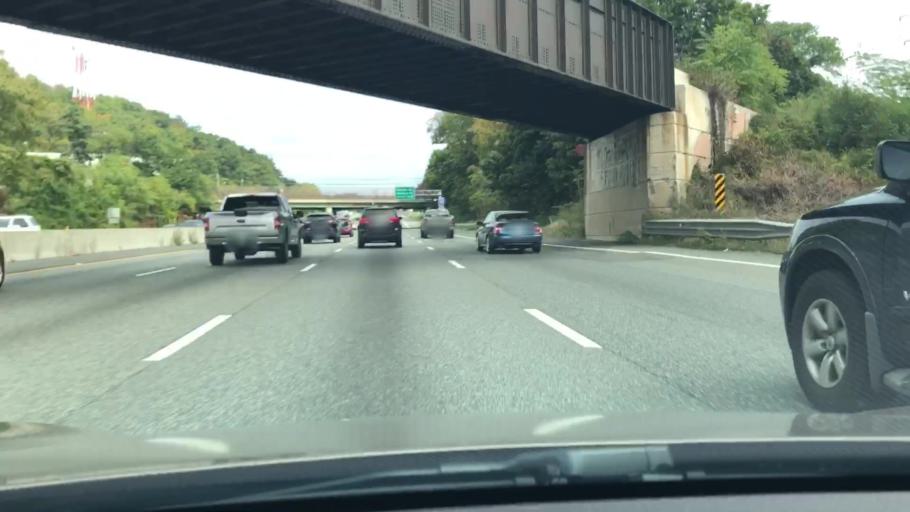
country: US
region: Massachusetts
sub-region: Middlesex County
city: Waltham
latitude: 42.3751
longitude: -71.2673
